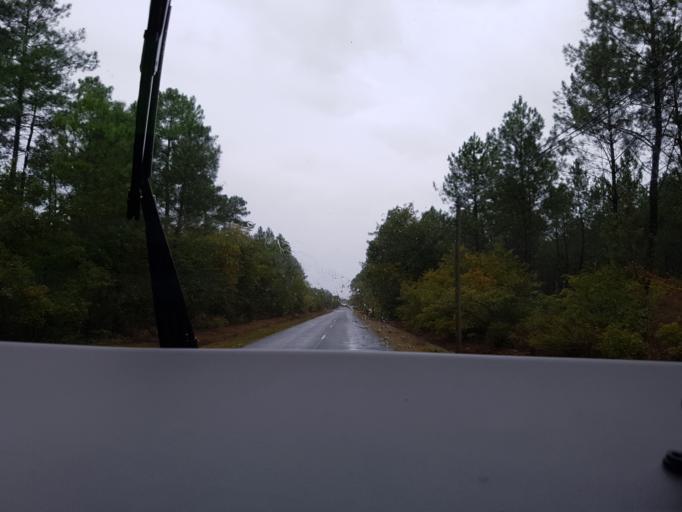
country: FR
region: Aquitaine
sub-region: Departement de la Gironde
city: Saint-Symphorien
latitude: 44.3519
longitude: -0.6217
